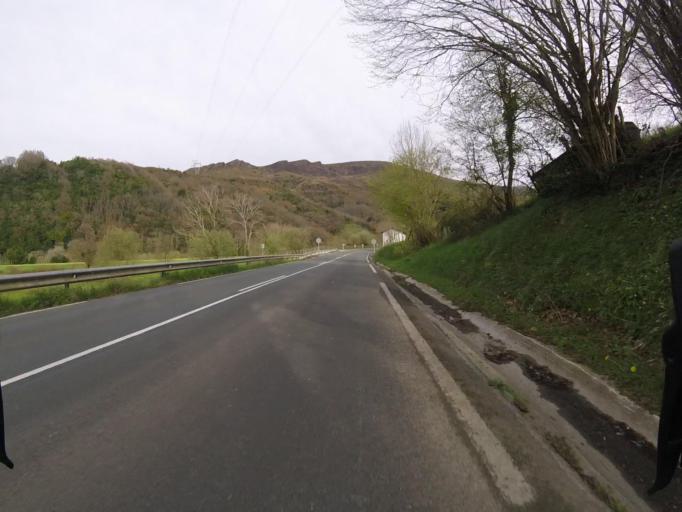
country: ES
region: Basque Country
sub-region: Provincia de Guipuzcoa
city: Irun
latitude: 43.3294
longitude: -1.7412
